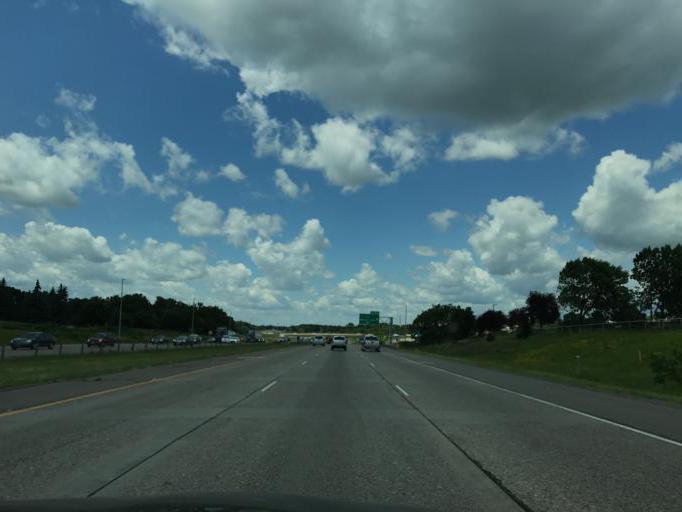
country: US
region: Minnesota
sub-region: Hennepin County
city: Maple Grove
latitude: 45.1009
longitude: -93.4553
